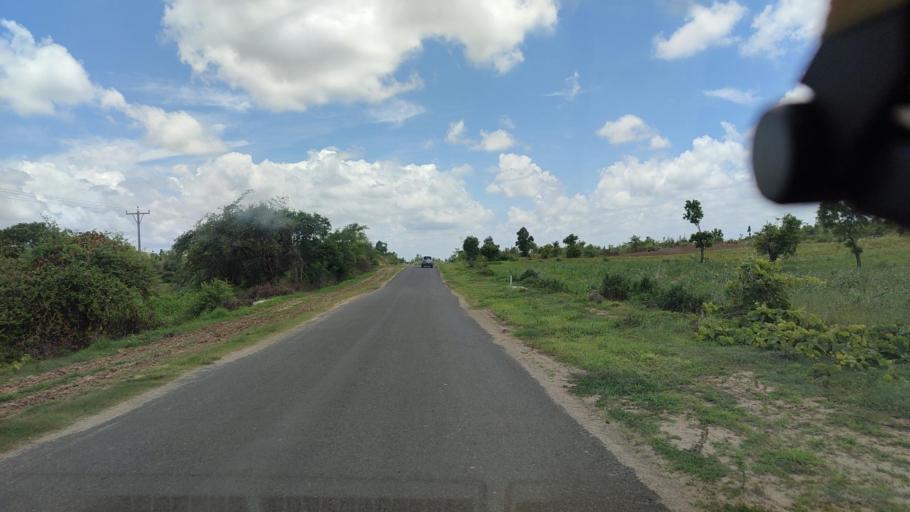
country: MM
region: Magway
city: Taungdwingyi
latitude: 20.1523
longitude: 95.5558
